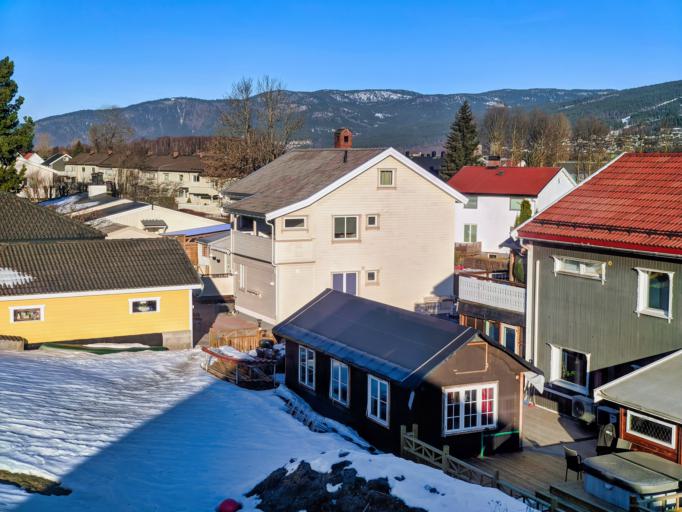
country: NO
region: Buskerud
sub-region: Drammen
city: Drammen
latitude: 59.7403
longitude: 10.1602
